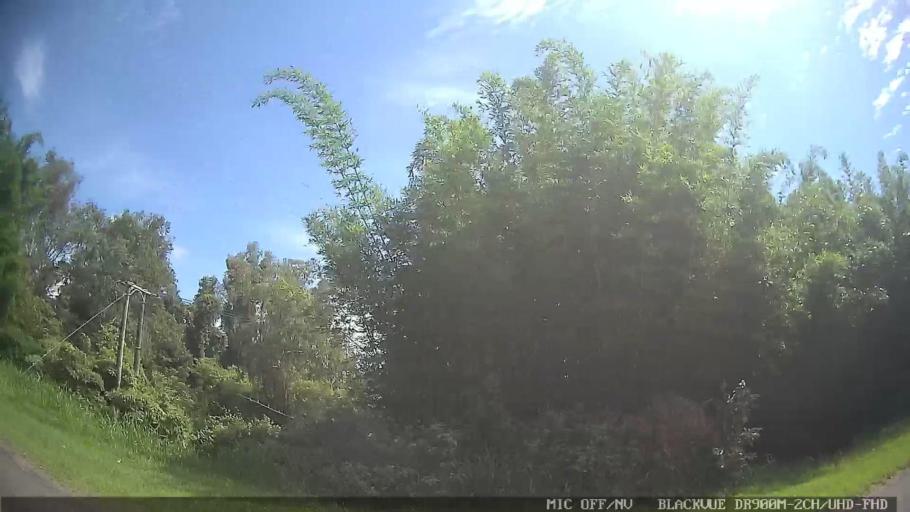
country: BR
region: Sao Paulo
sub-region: Porto Feliz
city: Porto Feliz
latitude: -23.2277
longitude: -47.5663
